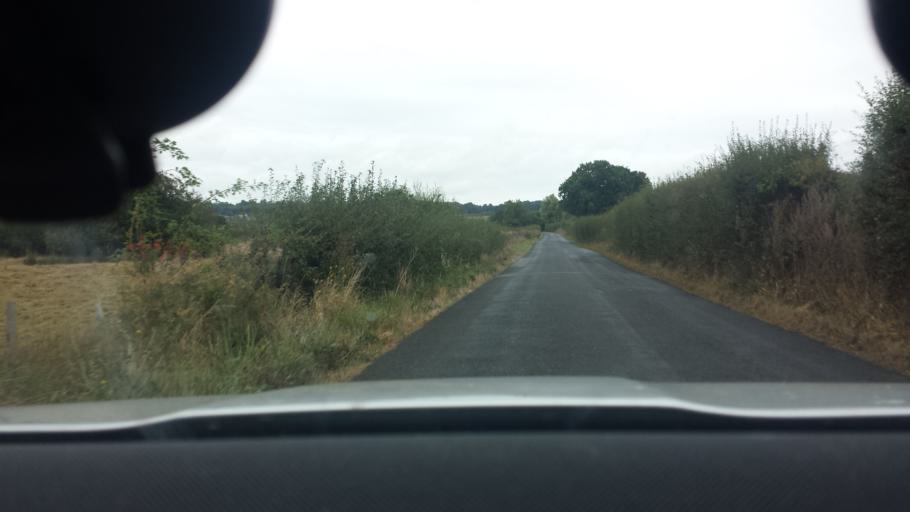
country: GB
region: England
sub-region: Kent
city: Staplehurst
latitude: 51.1992
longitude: 0.5546
